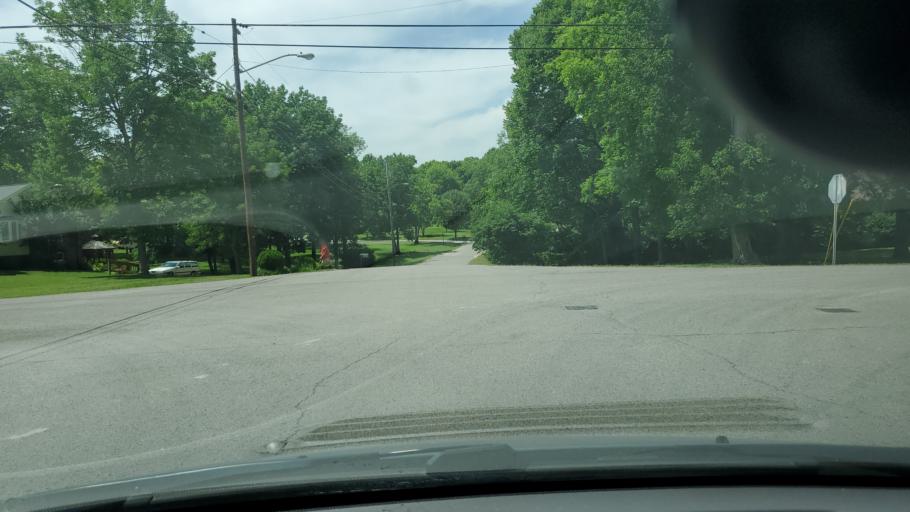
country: US
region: Tennessee
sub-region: Davidson County
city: Nashville
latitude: 36.2339
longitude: -86.7351
